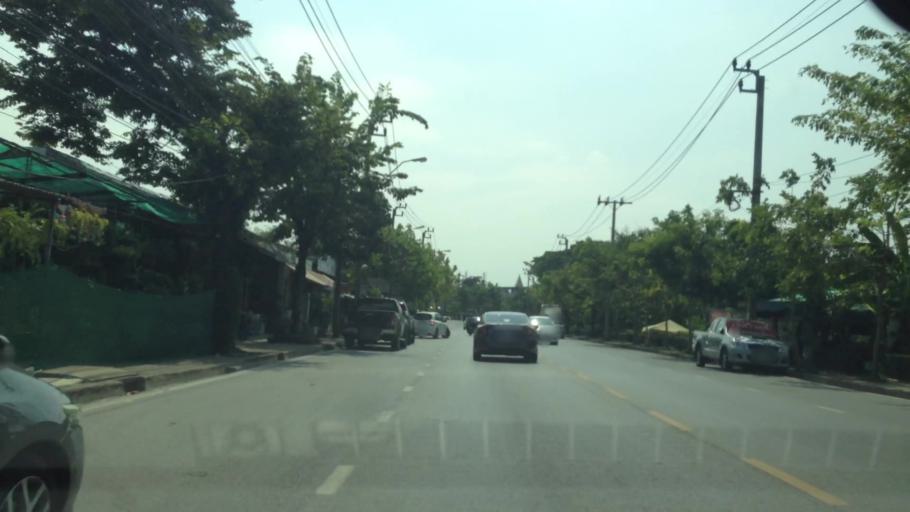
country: TH
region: Bangkok
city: Bang Khen
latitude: 13.8843
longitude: 100.6437
